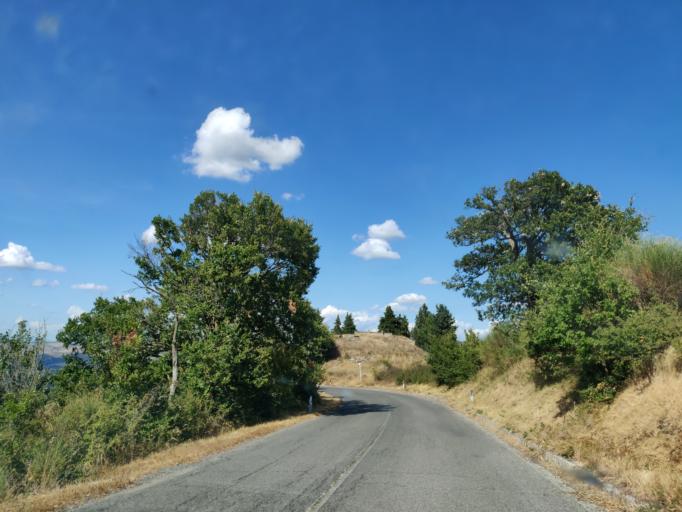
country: IT
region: Tuscany
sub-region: Provincia di Siena
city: Radicofani
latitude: 42.9697
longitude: 11.7358
